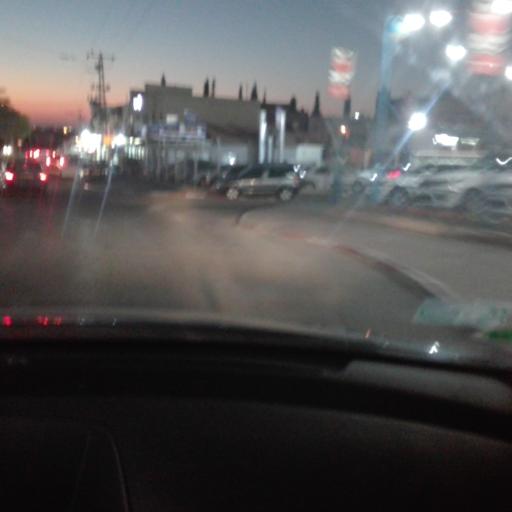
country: PS
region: West Bank
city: Nazlat `Isa
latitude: 32.4263
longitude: 35.0333
